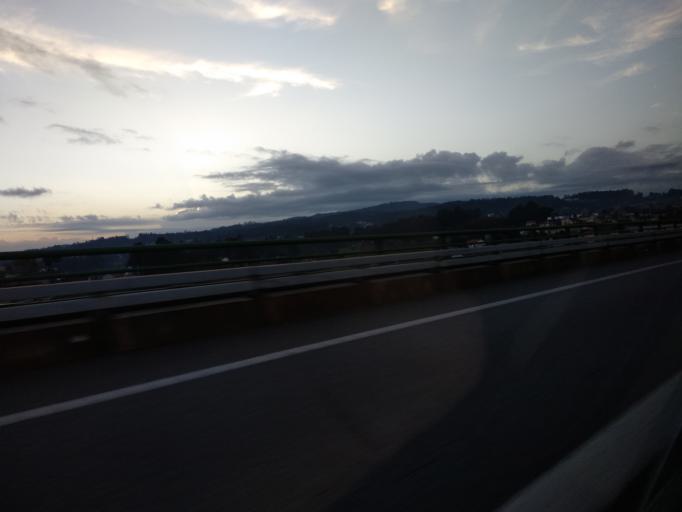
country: PT
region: Braga
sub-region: Braga
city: Oliveira
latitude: 41.4996
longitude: -8.4713
